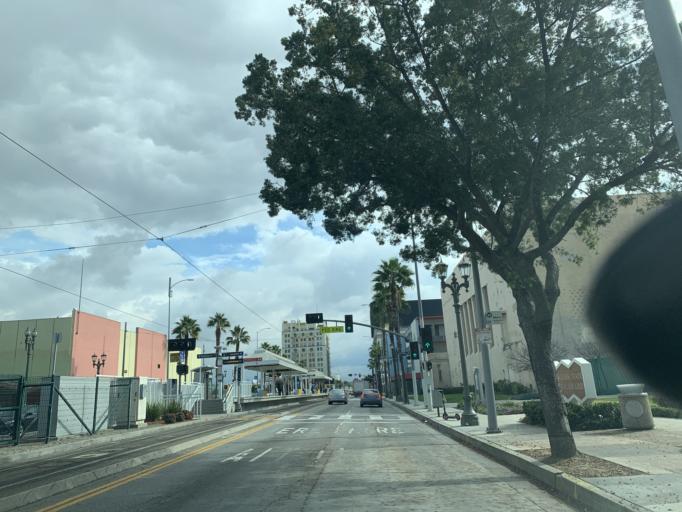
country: US
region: California
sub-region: Los Angeles County
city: Los Angeles
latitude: 34.0334
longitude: -118.2701
